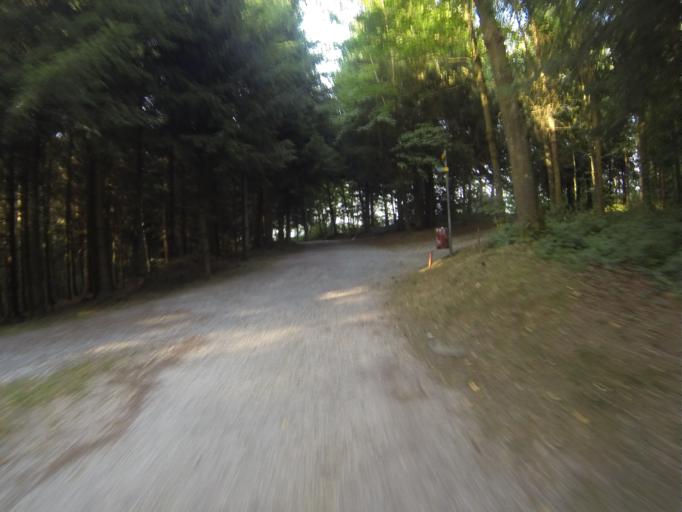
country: CH
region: Lucerne
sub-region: Lucerne-Land District
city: Buchrain
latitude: 47.0912
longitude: 8.3413
